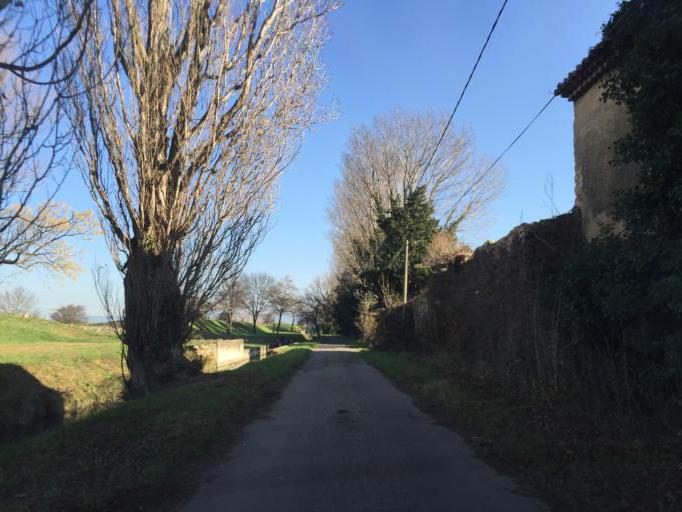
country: FR
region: Provence-Alpes-Cote d'Azur
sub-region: Departement du Vaucluse
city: Camaret-sur-Aigues
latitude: 44.1270
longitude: 4.8541
